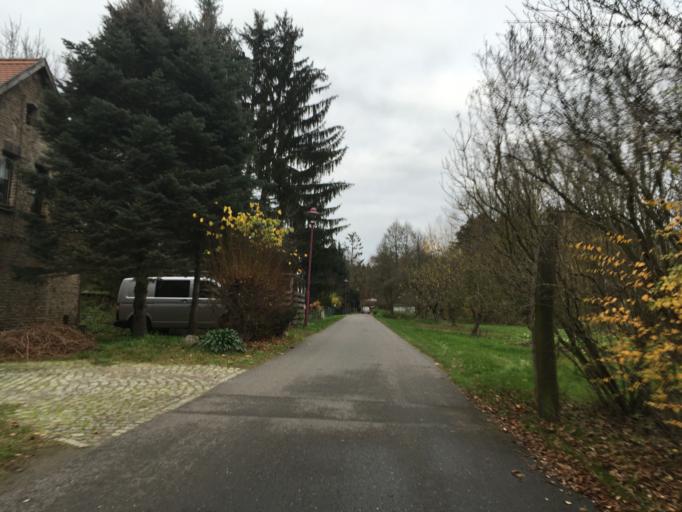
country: DE
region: Brandenburg
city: Mullrose
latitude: 52.2455
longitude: 14.4526
